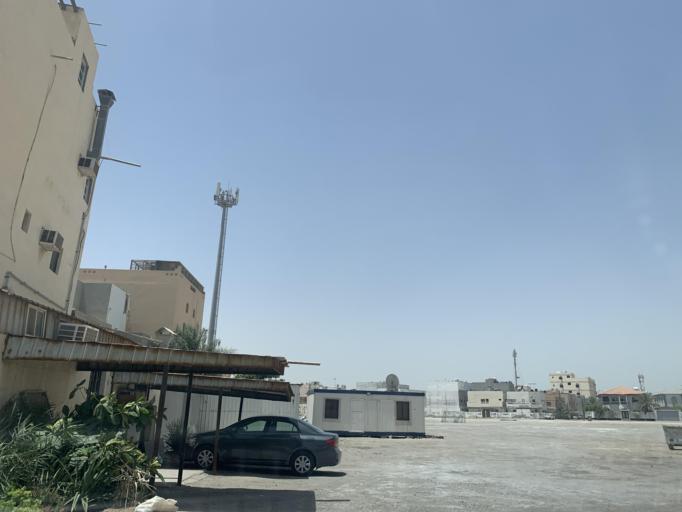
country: BH
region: Northern
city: Sitrah
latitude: 26.1609
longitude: 50.6216
